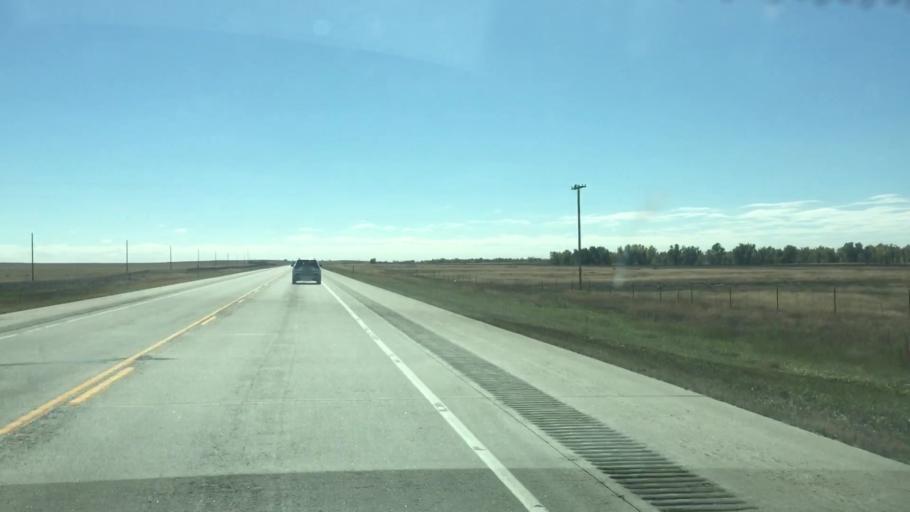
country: US
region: Colorado
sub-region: Lincoln County
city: Limon
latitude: 39.2379
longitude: -103.6230
